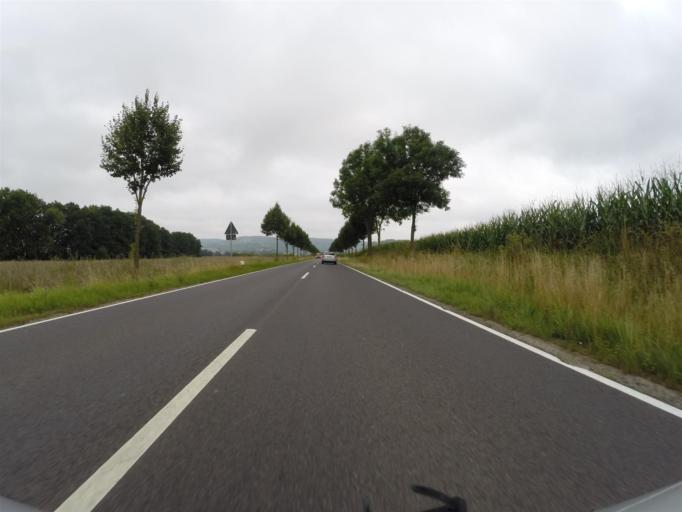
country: DE
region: Thuringia
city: Creuzburg
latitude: 51.0342
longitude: 10.2520
